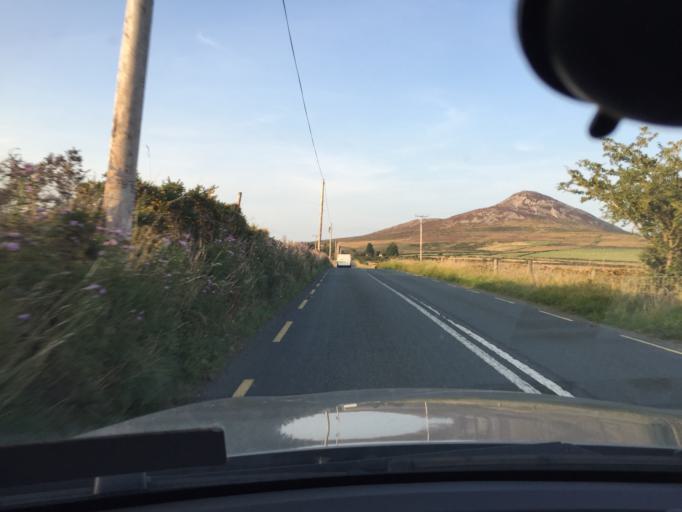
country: IE
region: Leinster
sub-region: Wicklow
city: Kilmacanoge
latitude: 53.1427
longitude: -6.1689
